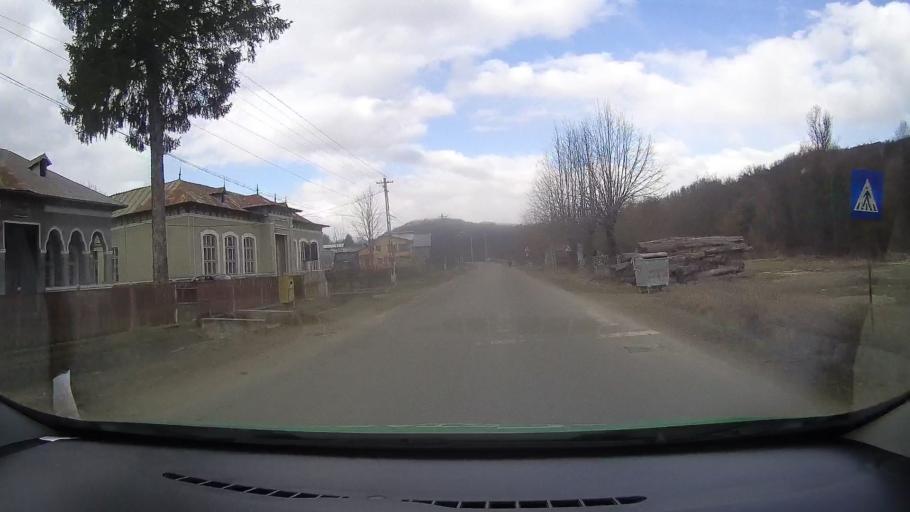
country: RO
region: Dambovita
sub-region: Comuna Valea Lunga
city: Valea Lunga-Cricov
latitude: 45.0648
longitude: 25.5575
